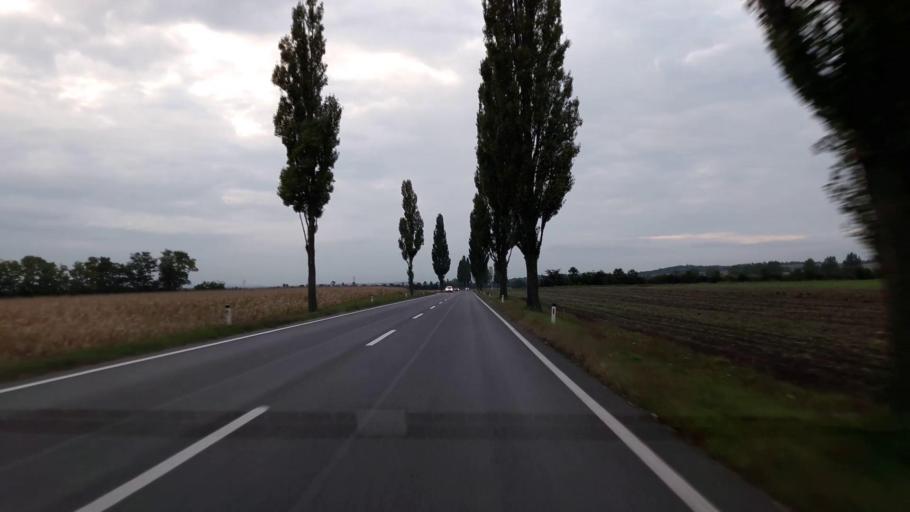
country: AT
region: Lower Austria
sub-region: Politischer Bezirk Bruck an der Leitha
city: Trautmannsdorf an der Leitha
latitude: 48.0420
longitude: 16.6668
